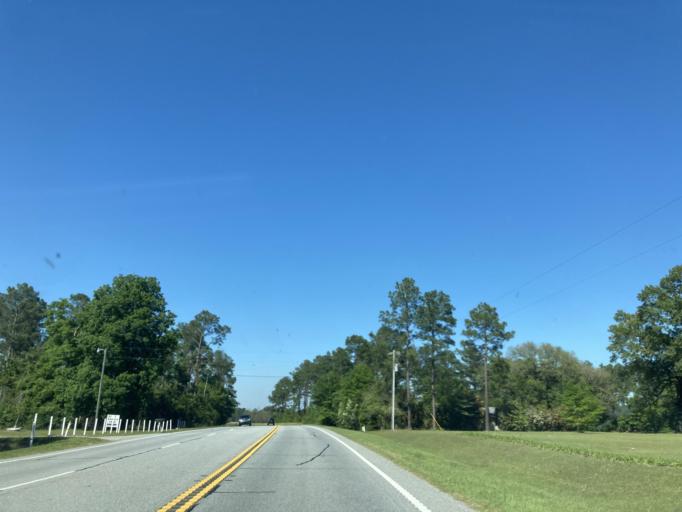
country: US
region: Georgia
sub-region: Baker County
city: Newton
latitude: 31.2957
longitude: -84.3481
